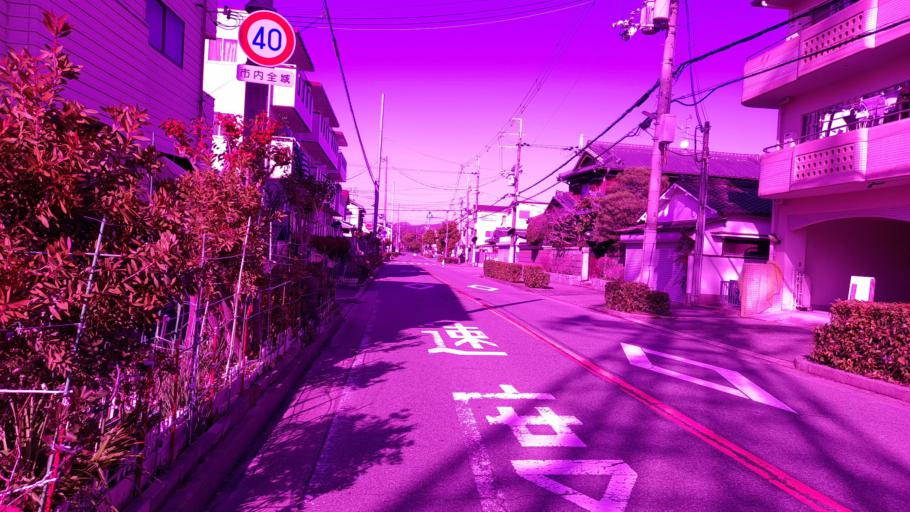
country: JP
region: Osaka
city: Toyonaka
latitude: 34.7620
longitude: 135.4479
